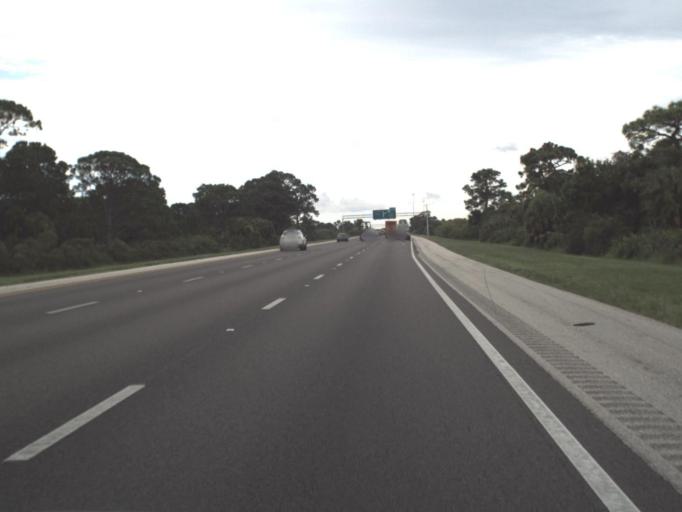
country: US
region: Florida
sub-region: Sarasota County
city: Osprey
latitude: 27.2024
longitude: -82.4419
